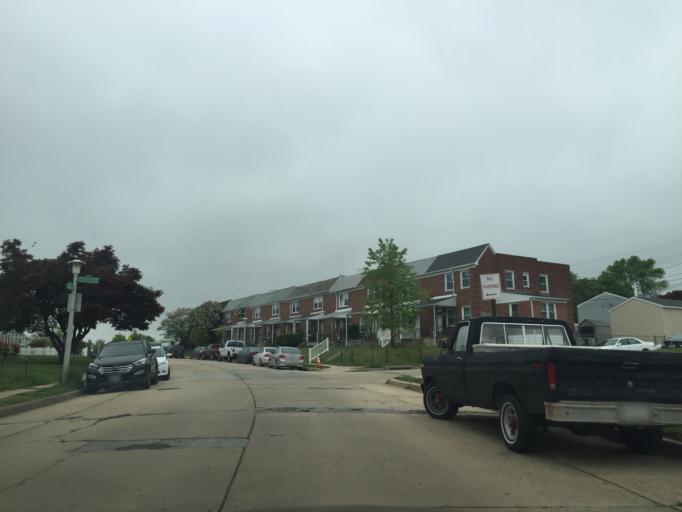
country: US
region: Maryland
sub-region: City of Baltimore
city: Baltimore
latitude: 39.3398
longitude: -76.6402
